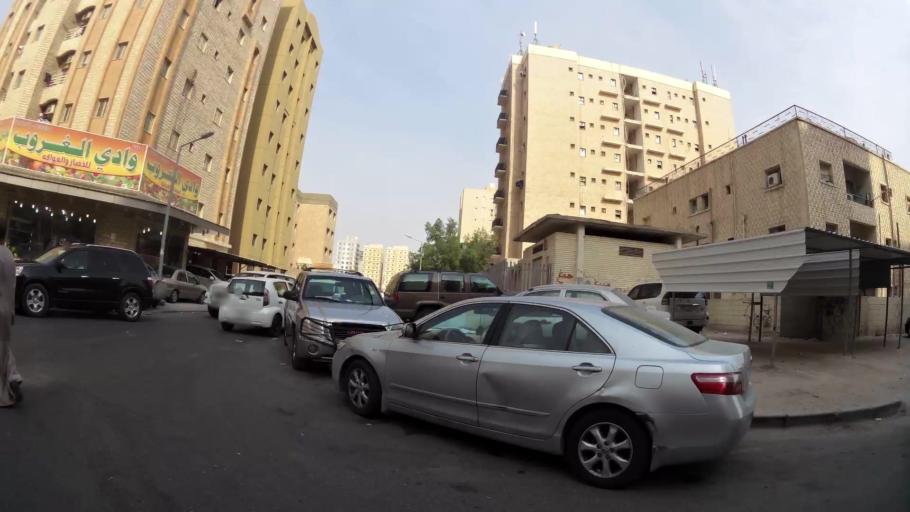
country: KW
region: Al Farwaniyah
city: Al Farwaniyah
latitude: 29.2739
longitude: 47.9564
